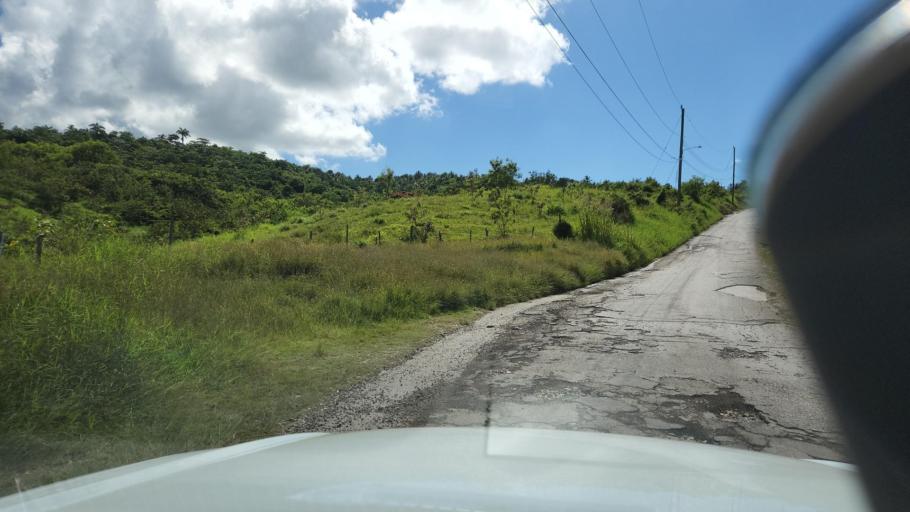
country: BB
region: Saint Thomas
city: Welchman Hall
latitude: 13.2130
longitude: -59.5568
